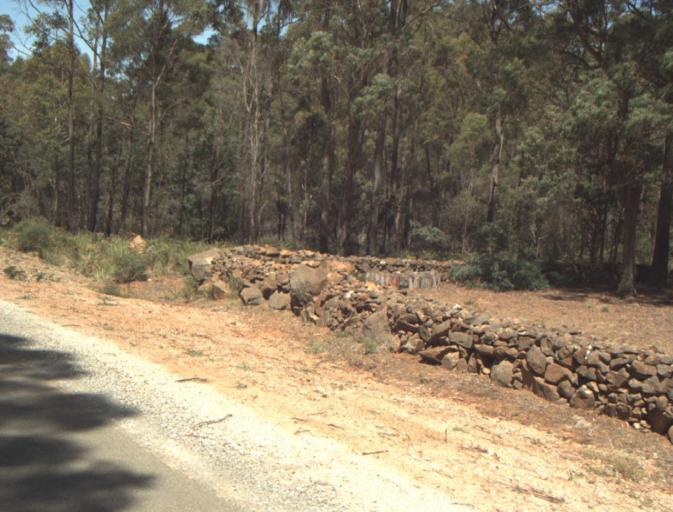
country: AU
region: Tasmania
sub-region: Launceston
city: Mayfield
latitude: -41.2811
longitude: 147.1194
